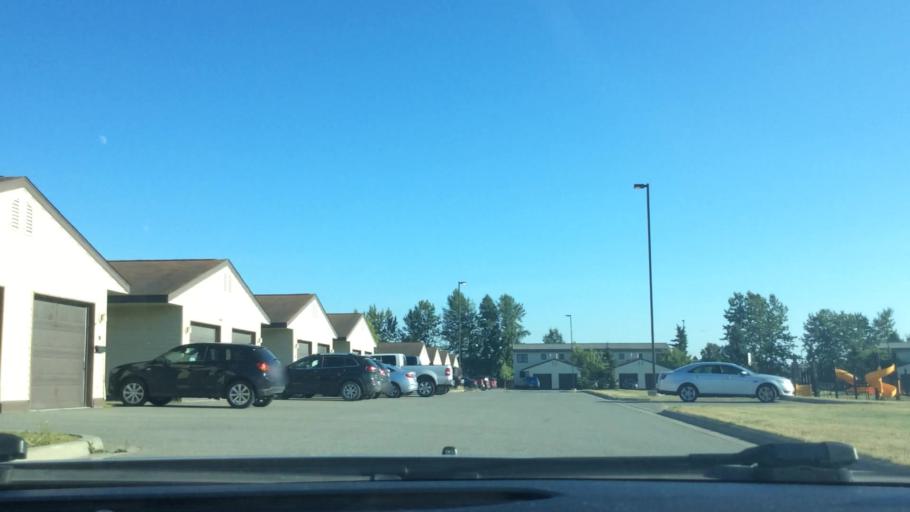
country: US
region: Alaska
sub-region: Anchorage Municipality
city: Anchorage
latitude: 61.2330
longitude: -149.8581
